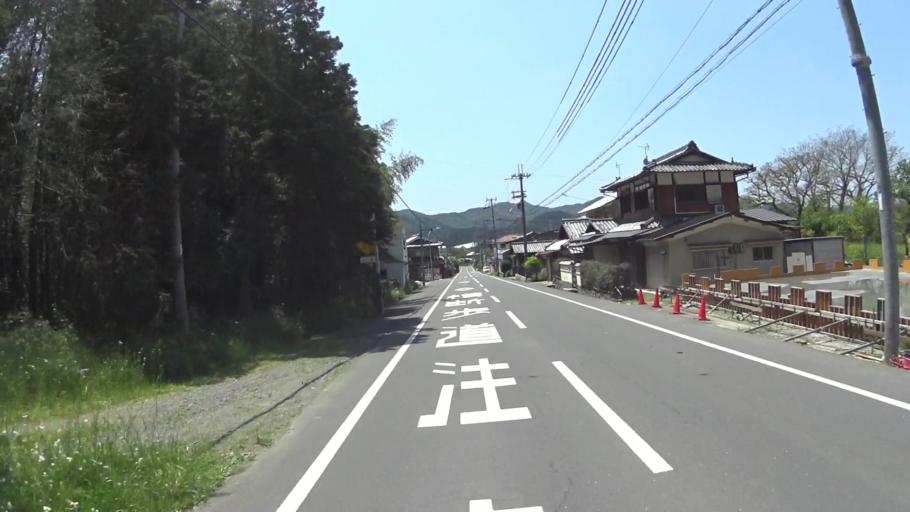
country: JP
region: Kyoto
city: Kameoka
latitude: 35.0762
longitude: 135.5434
